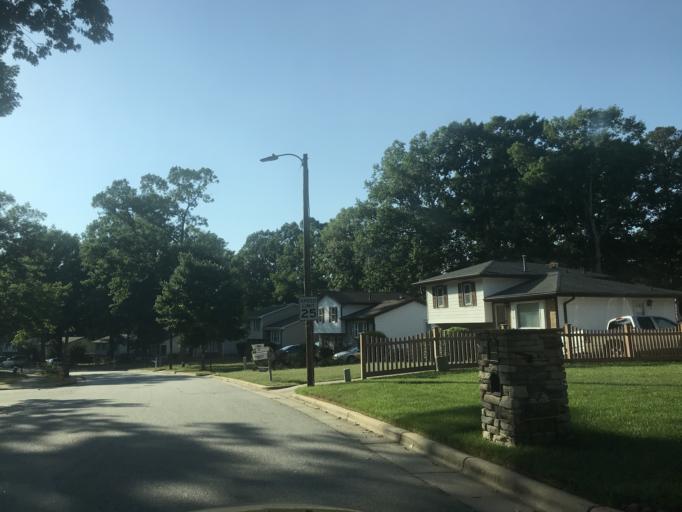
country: US
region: North Carolina
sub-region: Wake County
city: Garner
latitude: 35.7381
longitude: -78.6154
